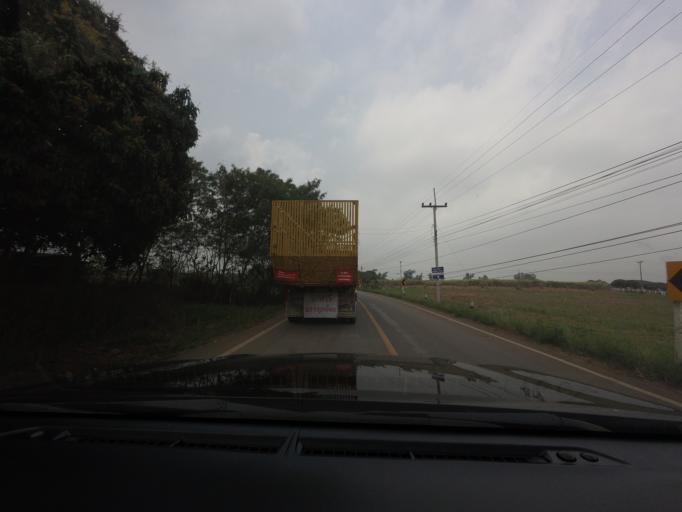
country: TH
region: Nakhon Ratchasima
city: Wang Nam Khiao
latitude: 14.4845
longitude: 101.6172
